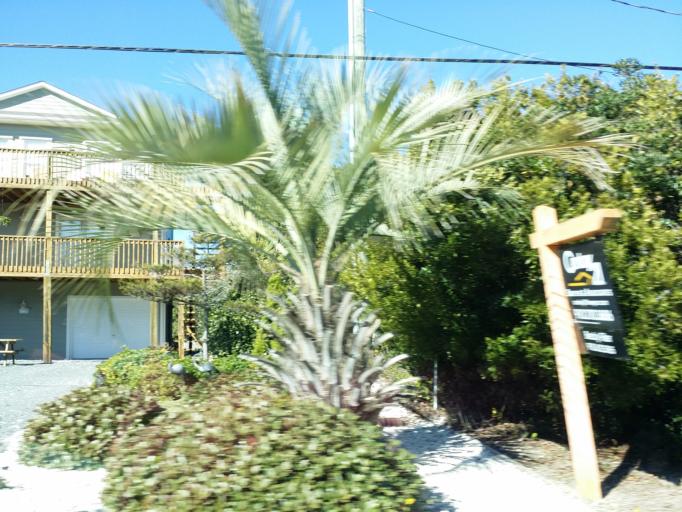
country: US
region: North Carolina
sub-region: Pender County
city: Surf City
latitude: 34.4183
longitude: -77.5572
